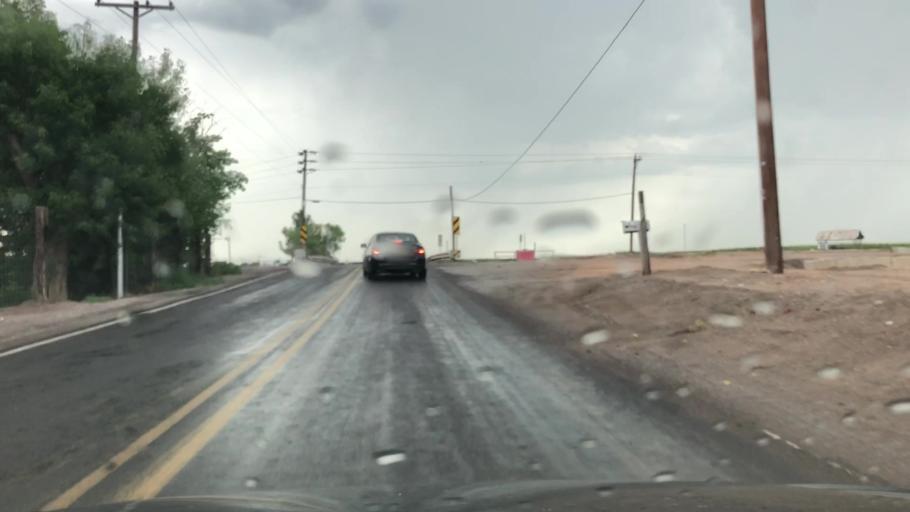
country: US
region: New Mexico
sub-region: Dona Ana County
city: Vado
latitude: 32.0609
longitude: -106.6772
